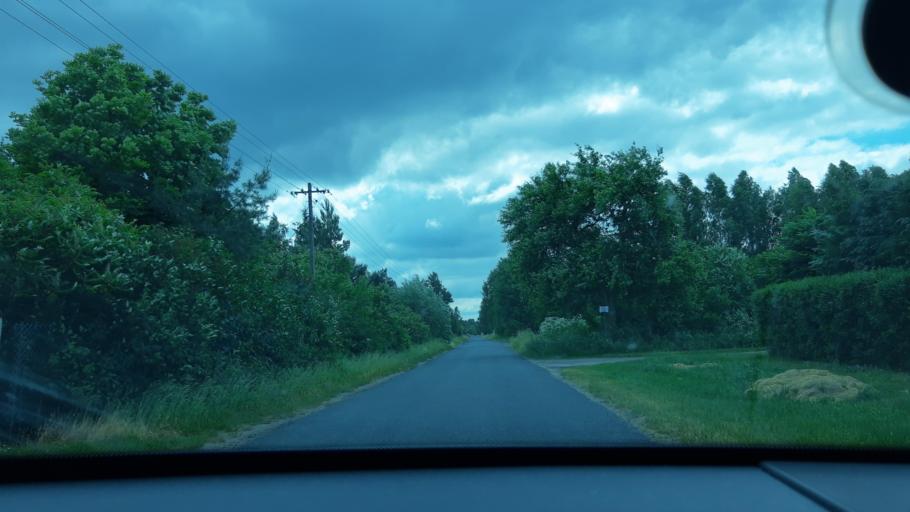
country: PL
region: Lodz Voivodeship
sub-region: Powiat zdunskowolski
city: Zapolice
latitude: 51.5210
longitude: 18.8438
